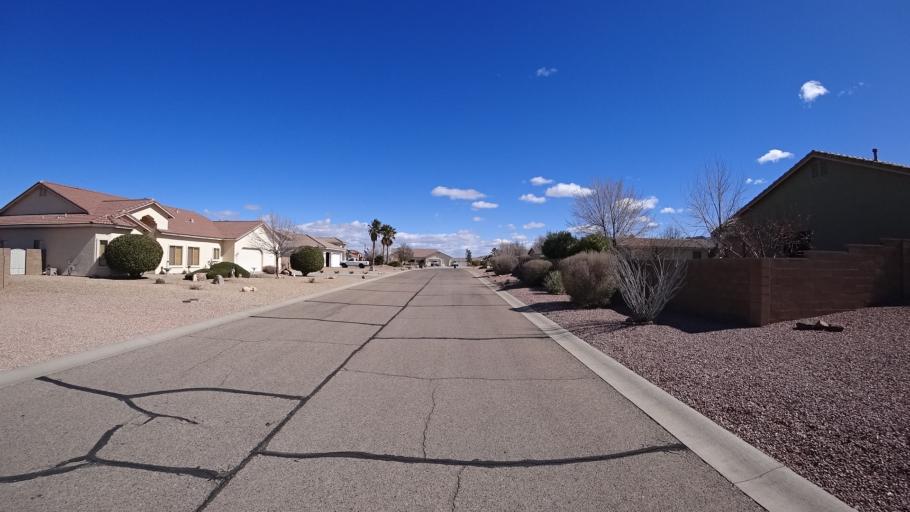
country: US
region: Arizona
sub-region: Mohave County
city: New Kingman-Butler
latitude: 35.2098
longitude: -113.9725
